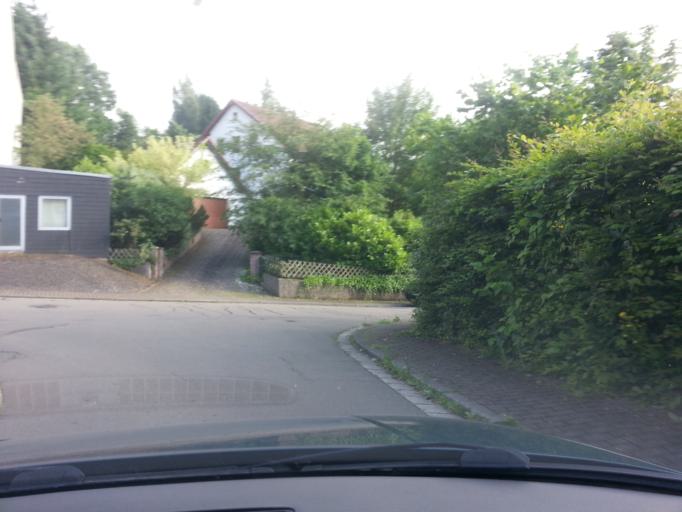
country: DE
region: Saarland
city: Marpingen
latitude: 49.4273
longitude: 7.0811
